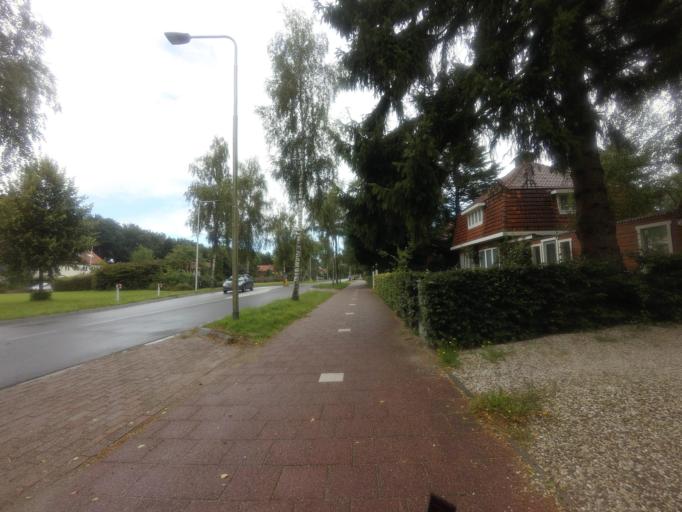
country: NL
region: North Holland
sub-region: Gemeente Wijdemeren
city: Nieuw-Loosdrecht
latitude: 52.1745
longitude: 5.1749
